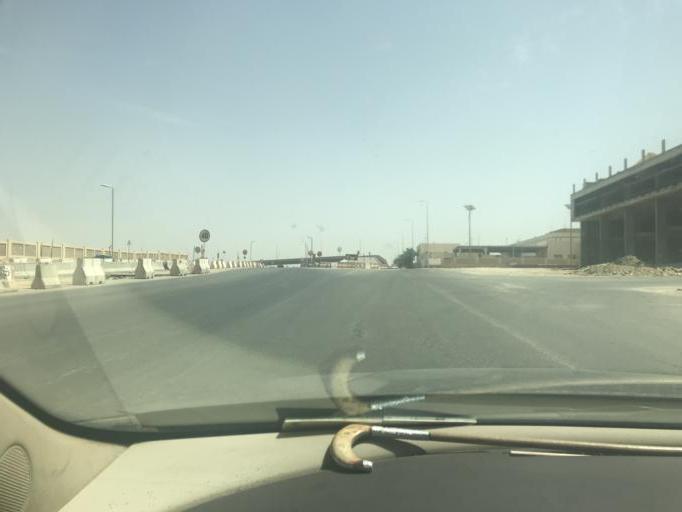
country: SA
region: Ar Riyad
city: Riyadh
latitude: 24.8321
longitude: 46.6929
